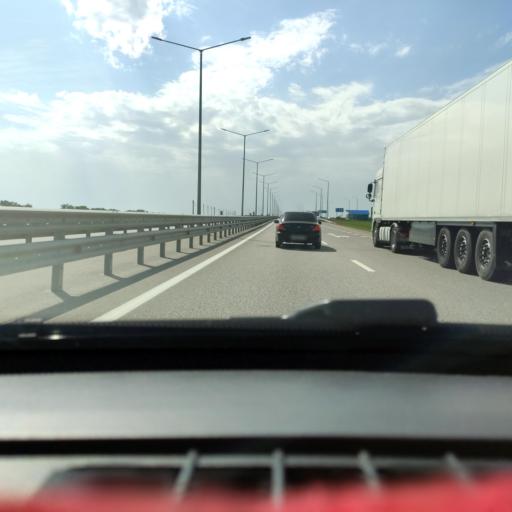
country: RU
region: Voronezj
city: Podkletnoye
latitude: 51.5452
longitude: 39.4965
